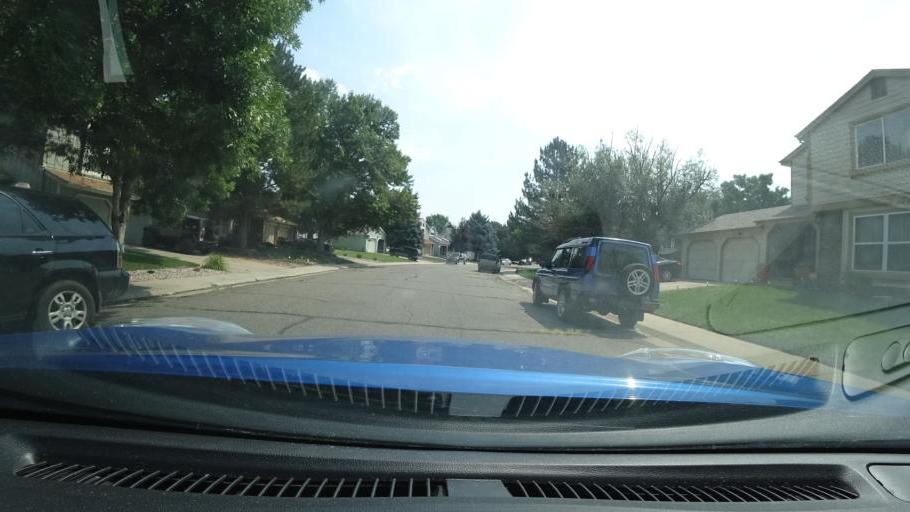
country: US
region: Colorado
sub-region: Adams County
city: Aurora
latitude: 39.7777
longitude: -104.7625
